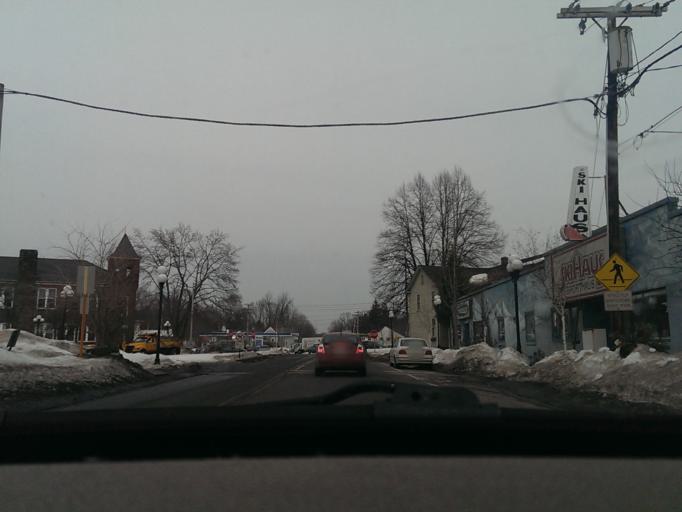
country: US
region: Massachusetts
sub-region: Hampden County
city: East Longmeadow
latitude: 42.0641
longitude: -72.5135
